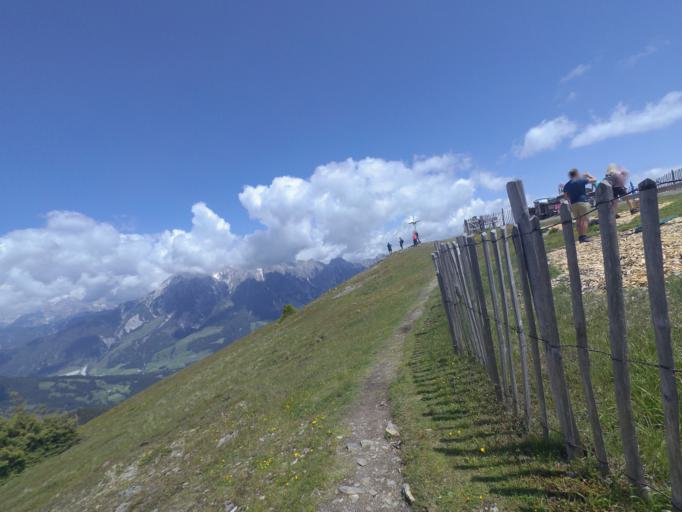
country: AT
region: Salzburg
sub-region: Politischer Bezirk Zell am See
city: Viehhofen
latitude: 47.4023
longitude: 12.7022
